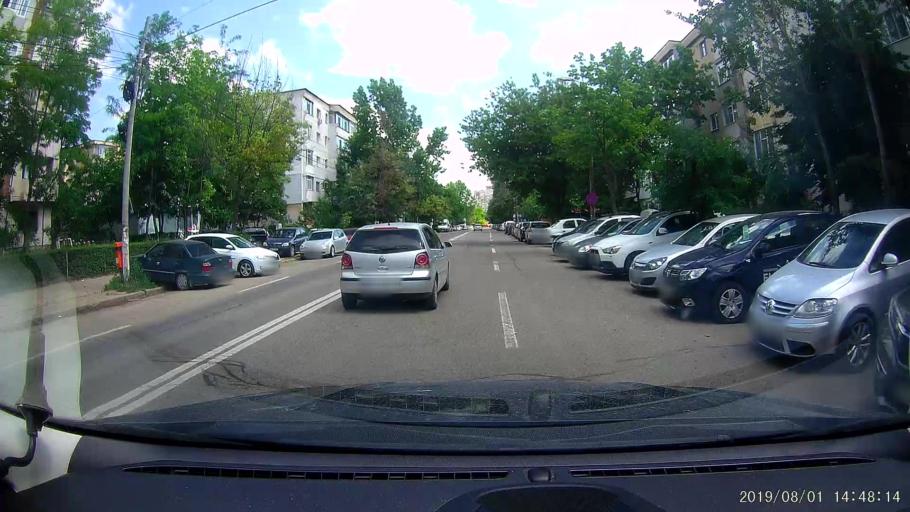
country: RO
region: Galati
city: Galati
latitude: 45.4118
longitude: 28.0077
